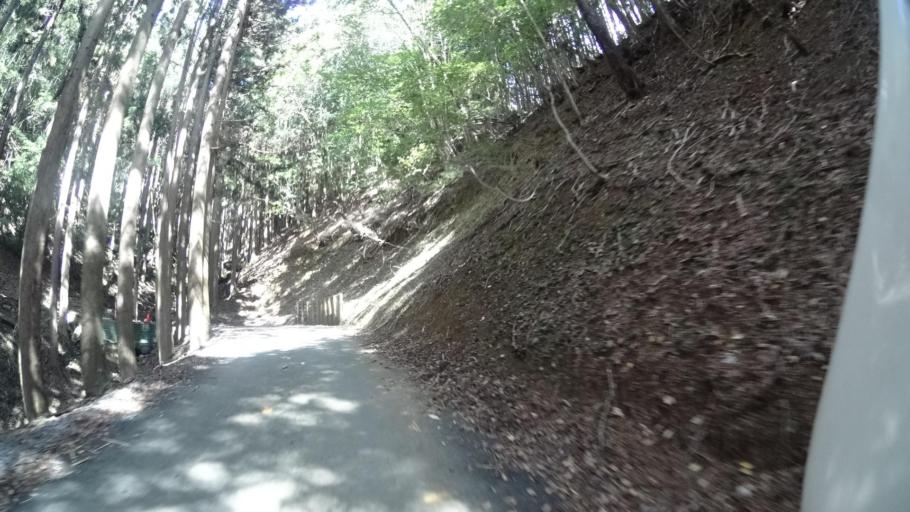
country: JP
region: Kyoto
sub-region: Kyoto-shi
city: Kamigyo-ku
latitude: 35.1478
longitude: 135.7597
